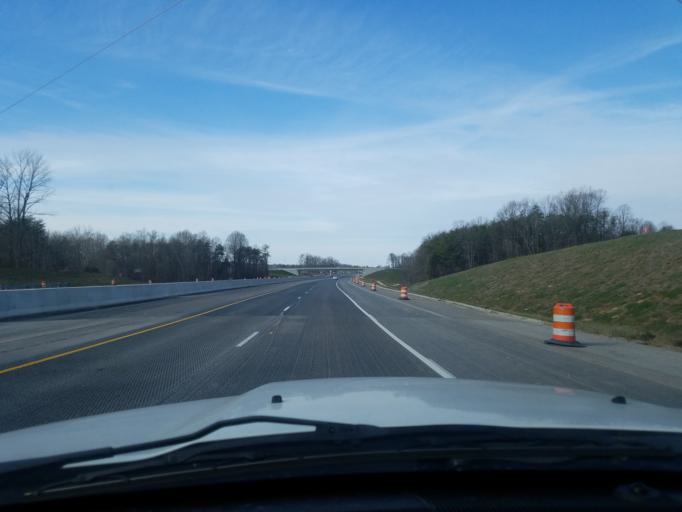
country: US
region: Indiana
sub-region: Monroe County
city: Bloomington
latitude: 39.1145
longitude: -86.5636
